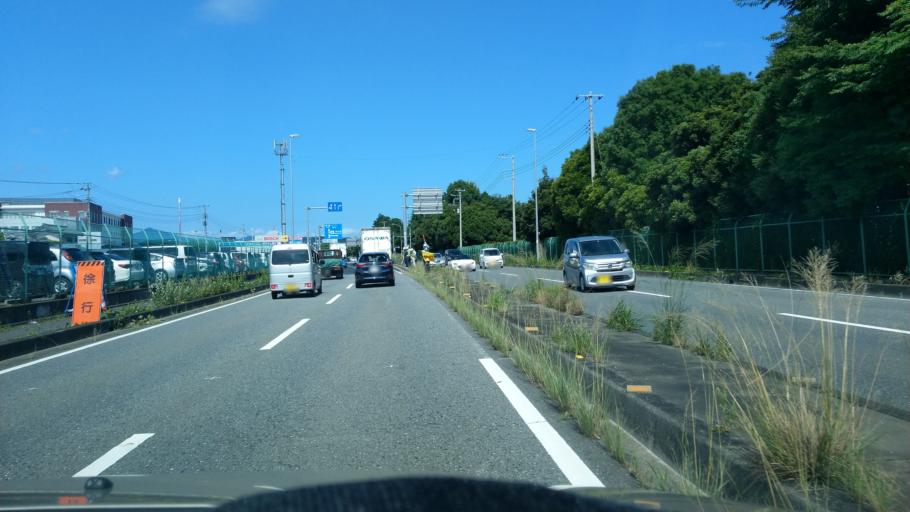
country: JP
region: Saitama
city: Ogawa
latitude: 36.0398
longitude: 139.3491
